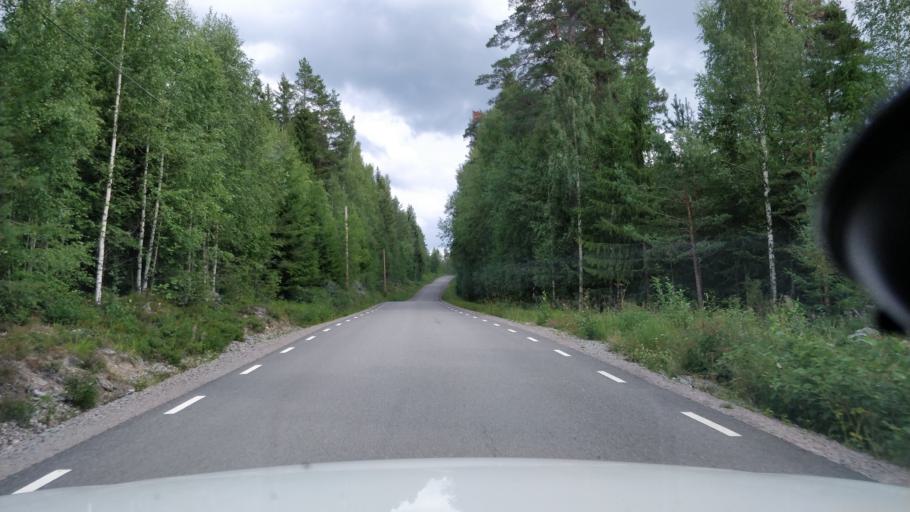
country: SE
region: Dalarna
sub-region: Faluns Kommun
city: Bjursas
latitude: 60.7441
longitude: 15.5539
